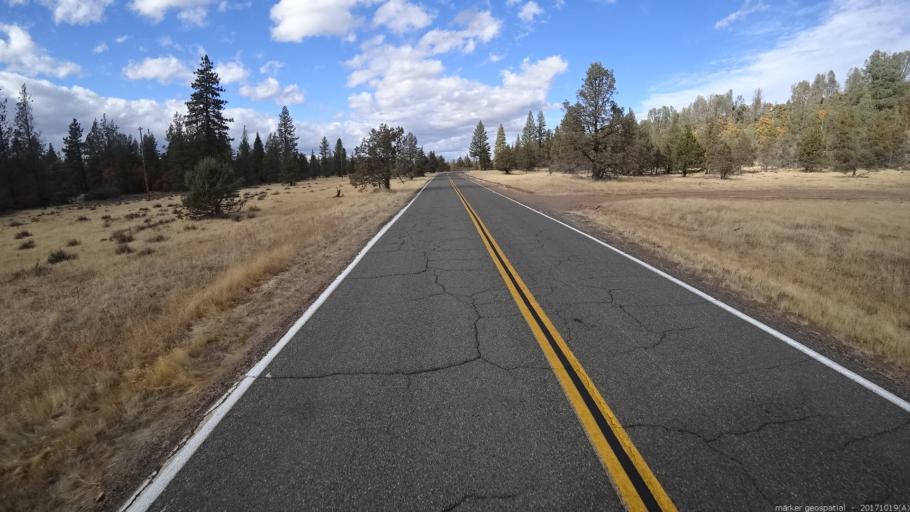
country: US
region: California
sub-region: Shasta County
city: Burney
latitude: 40.9824
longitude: -121.4336
